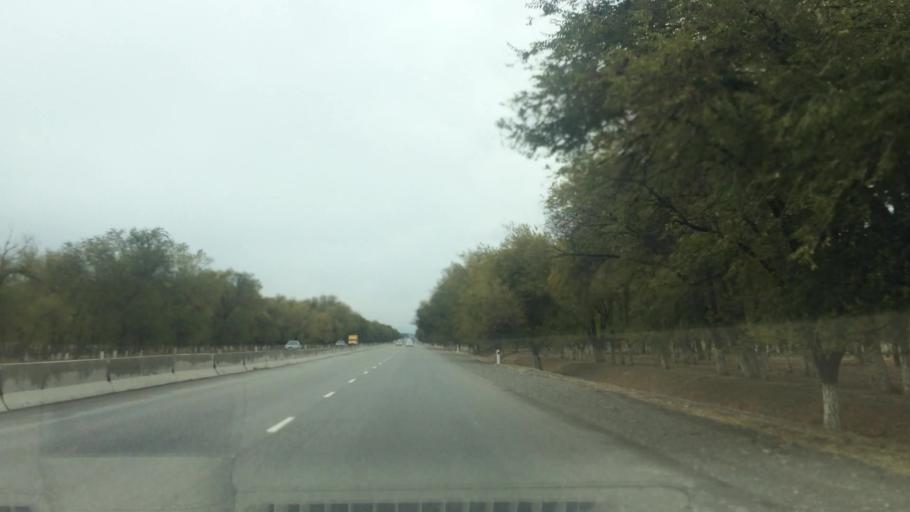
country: UZ
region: Samarqand
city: Bulung'ur
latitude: 39.7991
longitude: 67.3395
